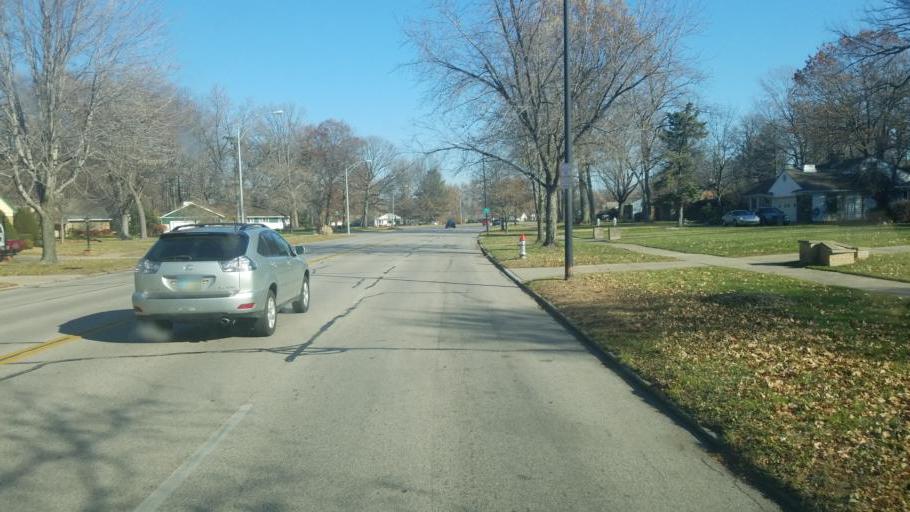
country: US
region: Ohio
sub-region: Cuyahoga County
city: Cleveland Heights
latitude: 41.5221
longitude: -81.5664
